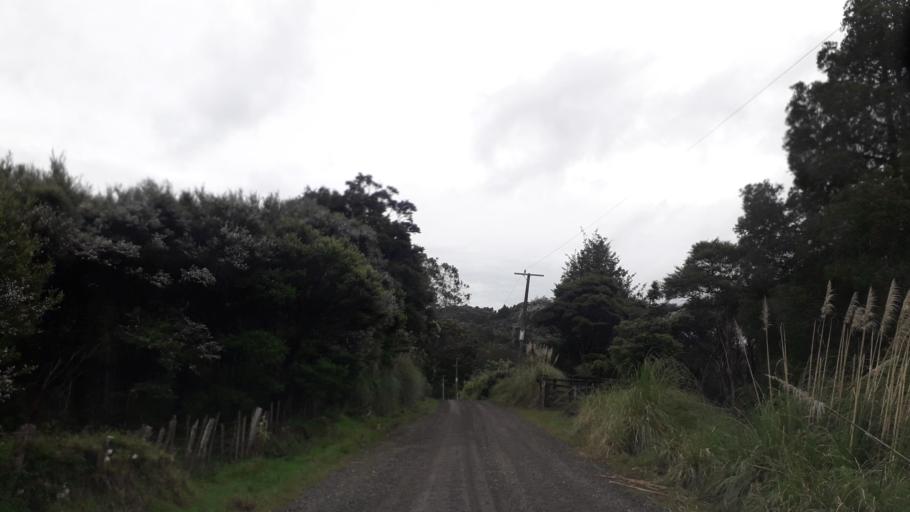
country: NZ
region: Northland
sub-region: Far North District
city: Kaitaia
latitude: -35.3854
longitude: 173.4063
